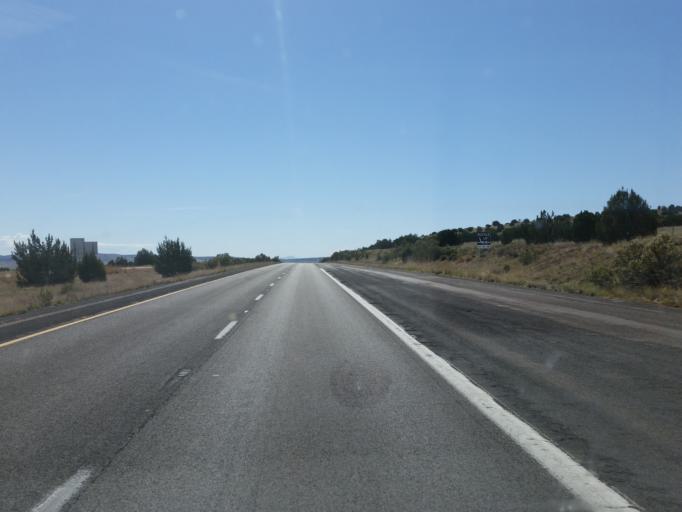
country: US
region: Arizona
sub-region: Mohave County
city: Peach Springs
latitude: 35.3195
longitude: -112.8904
